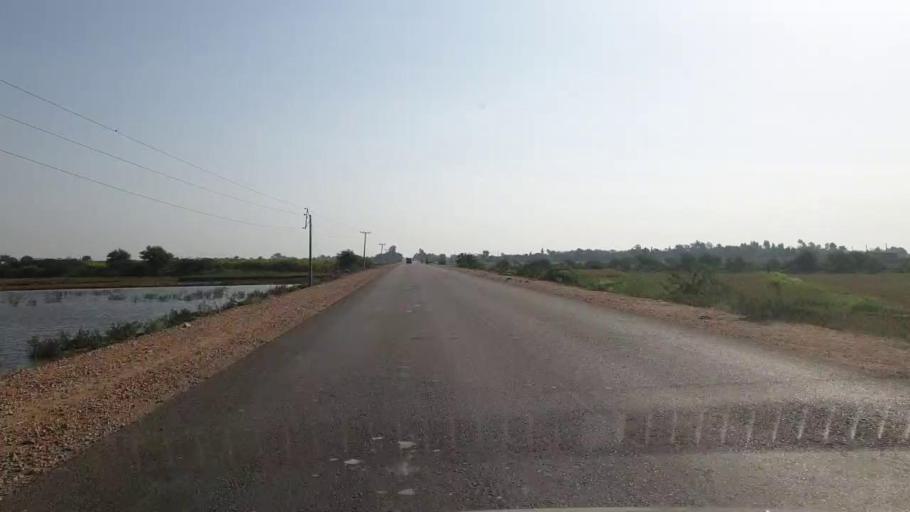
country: PK
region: Sindh
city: Badin
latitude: 24.6581
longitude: 68.9656
